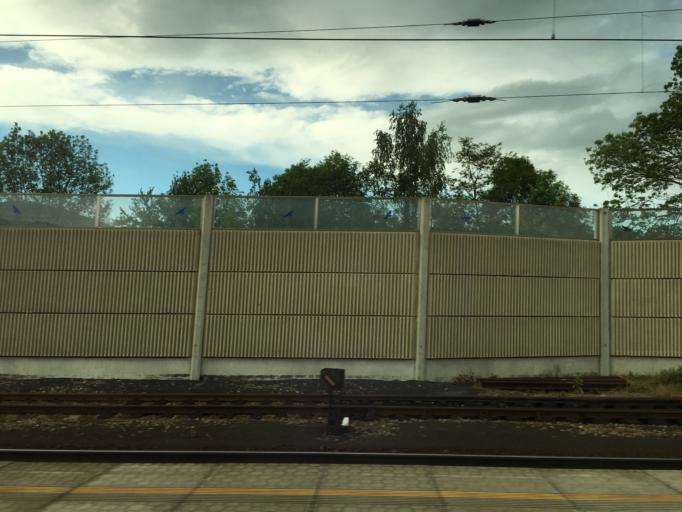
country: CZ
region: Ustecky
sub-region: Okres Usti nad Labem
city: Usti nad Labem
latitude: 50.6643
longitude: 14.0818
